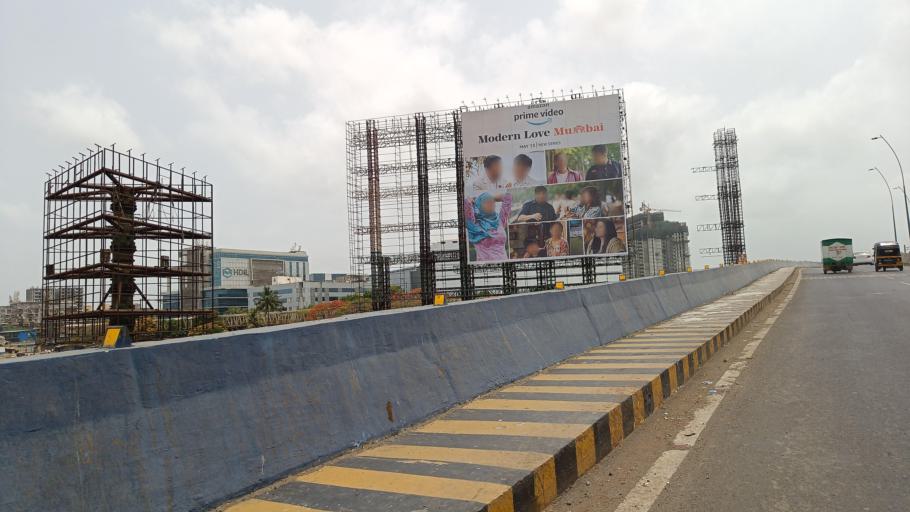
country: IN
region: Maharashtra
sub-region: Mumbai Suburban
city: Mumbai
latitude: 19.0522
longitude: 72.8434
